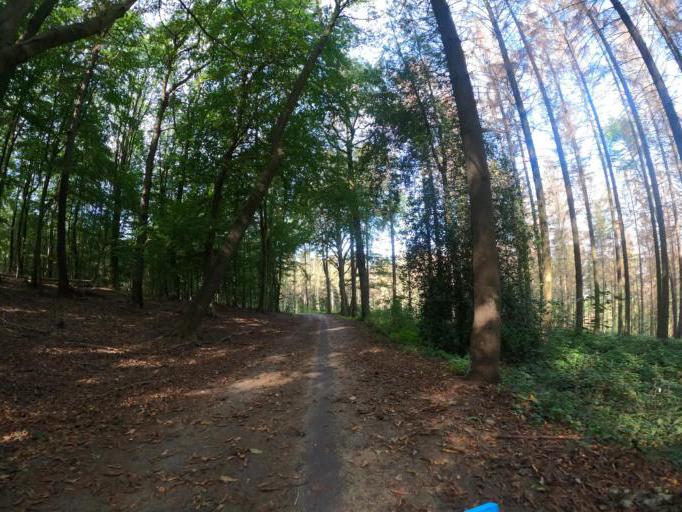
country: DE
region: North Rhine-Westphalia
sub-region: Regierungsbezirk Dusseldorf
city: Wuppertal
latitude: 51.2373
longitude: 7.1139
